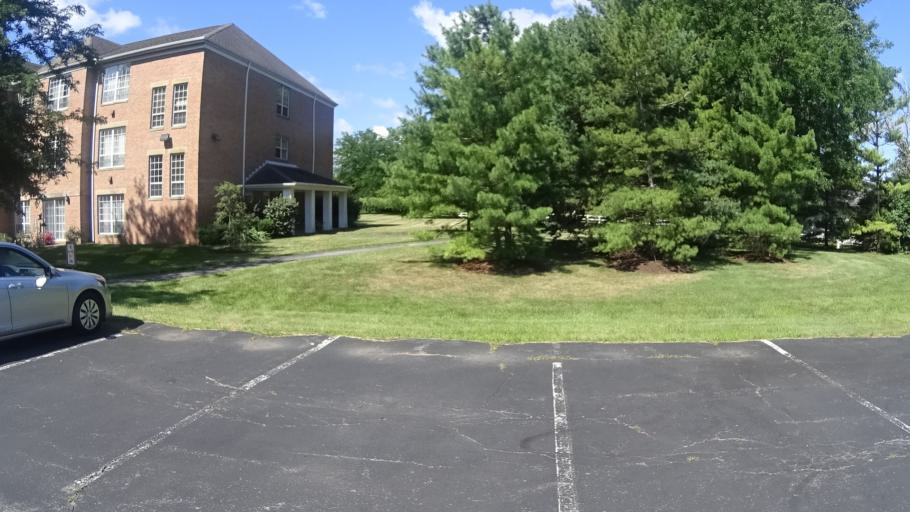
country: US
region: Ohio
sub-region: Erie County
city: Sandusky
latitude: 41.4117
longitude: -82.6590
